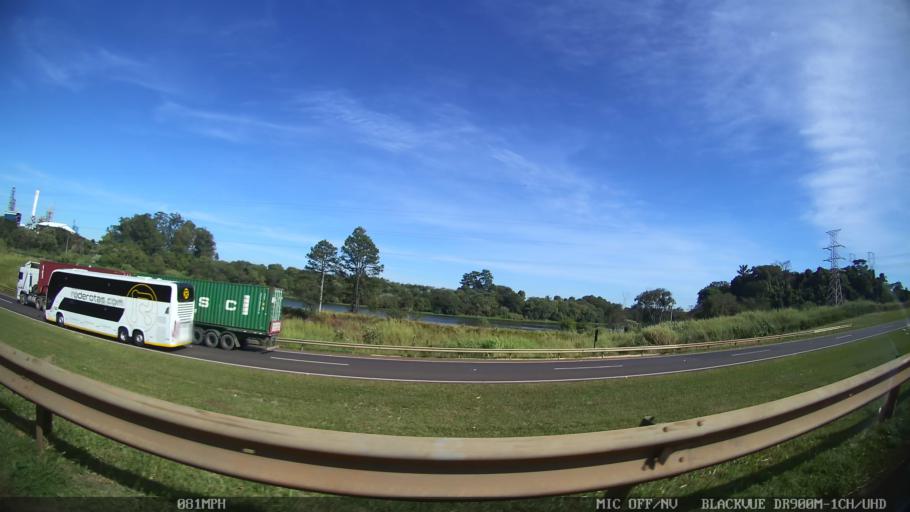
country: BR
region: Sao Paulo
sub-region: Araras
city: Araras
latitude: -22.2917
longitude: -47.3928
